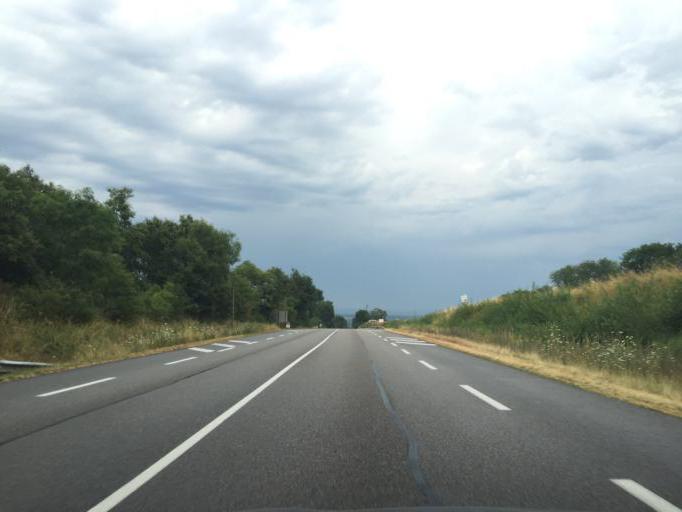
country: FR
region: Rhone-Alpes
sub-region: Departement de la Loire
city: La Pacaudiere
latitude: 46.1972
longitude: 3.8349
